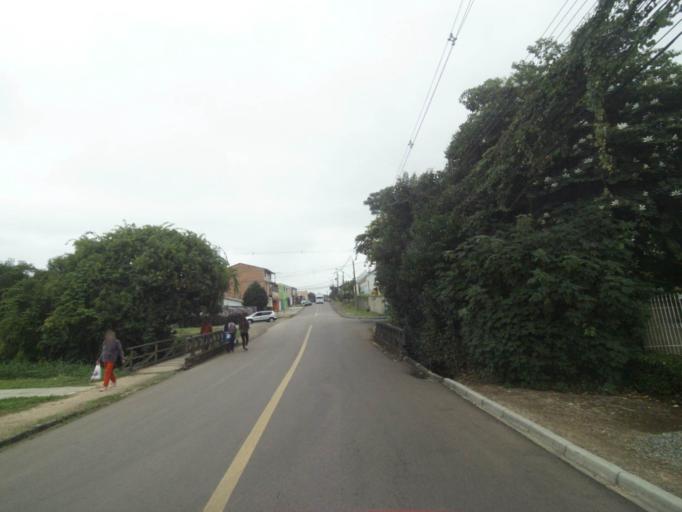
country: BR
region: Parana
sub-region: Curitiba
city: Curitiba
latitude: -25.4867
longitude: -49.3052
